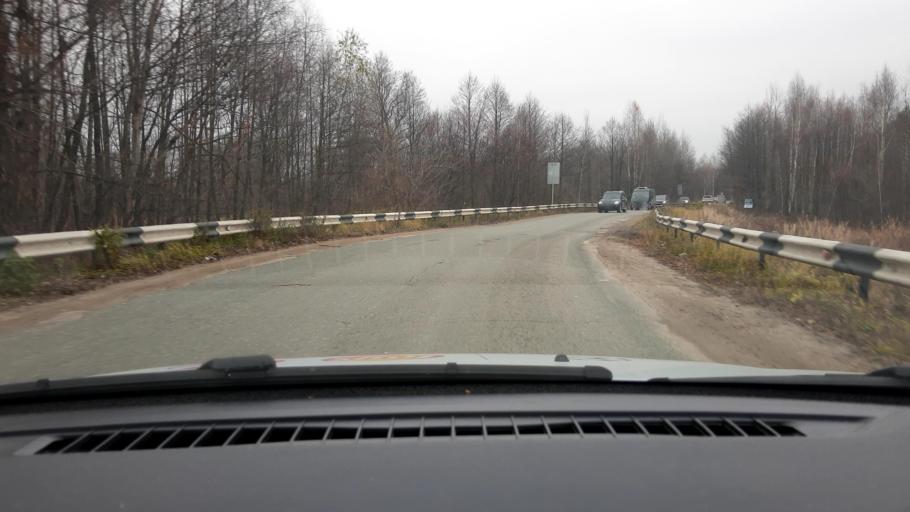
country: RU
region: Nizjnij Novgorod
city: Neklyudovo
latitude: 56.4236
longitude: 43.9247
